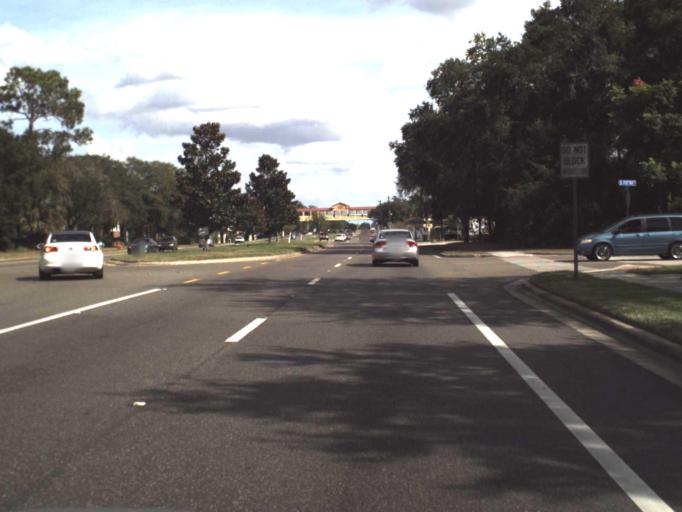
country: US
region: Florida
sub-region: Seminole County
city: Lake Mary
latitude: 28.7561
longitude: -81.3266
